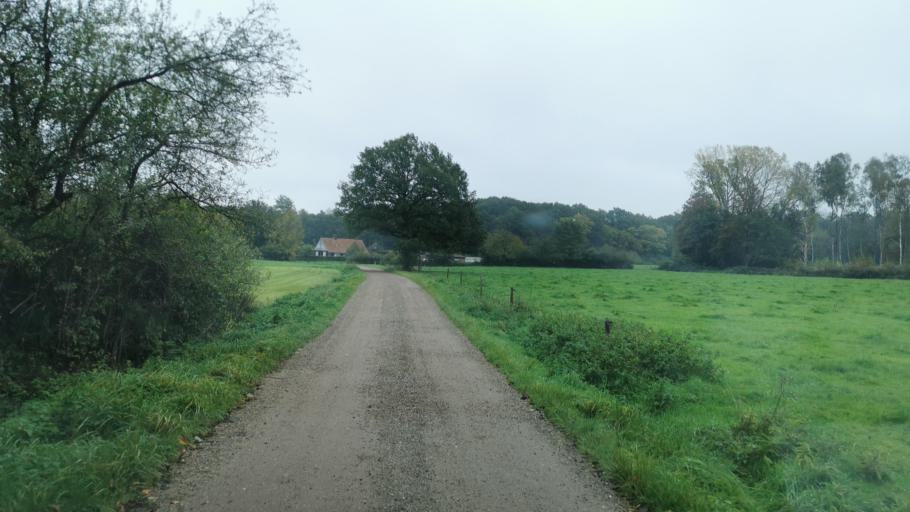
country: NL
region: Overijssel
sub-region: Gemeente Oldenzaal
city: Oldenzaal
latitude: 52.3339
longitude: 6.9674
